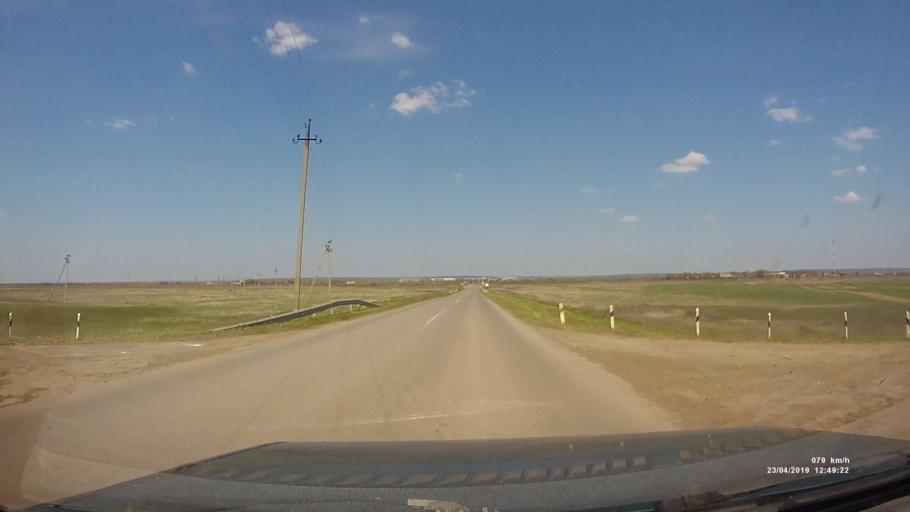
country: RU
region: Kalmykiya
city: Yashalta
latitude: 46.5364
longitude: 42.6391
